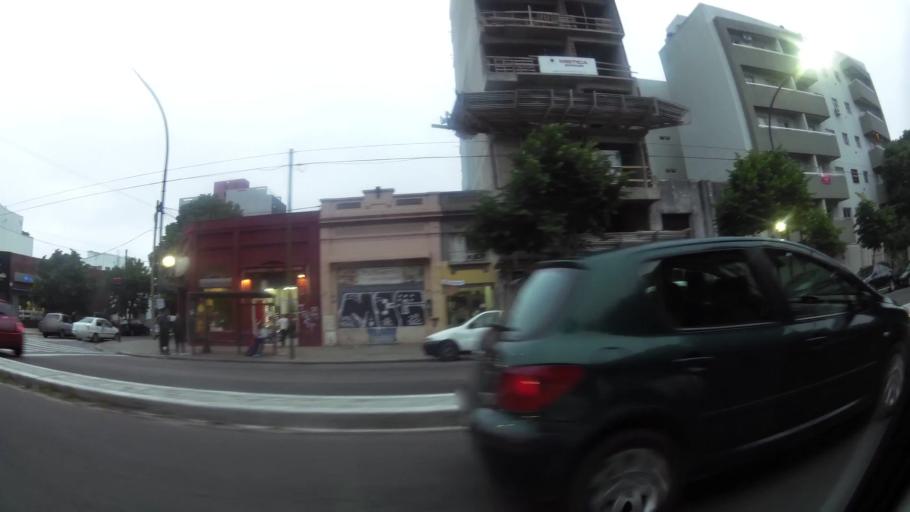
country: AR
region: Buenos Aires
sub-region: Partido de La Plata
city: La Plata
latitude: -34.9013
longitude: -57.9680
